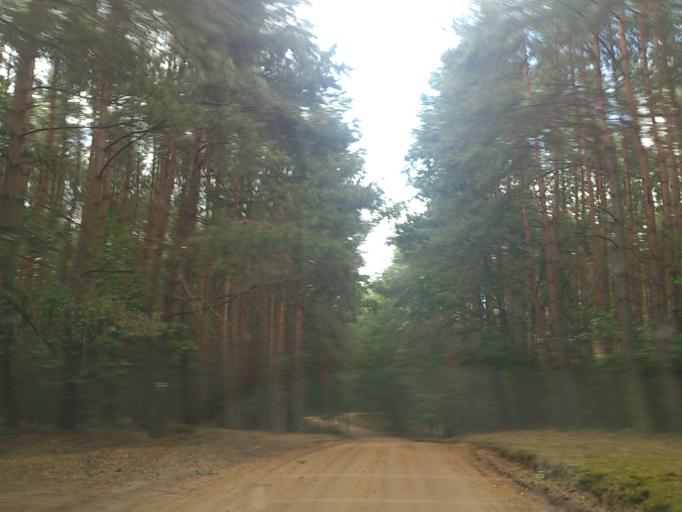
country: PL
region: Greater Poland Voivodeship
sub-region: Powiat poznanski
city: Kobylnica
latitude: 52.5307
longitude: 17.1160
